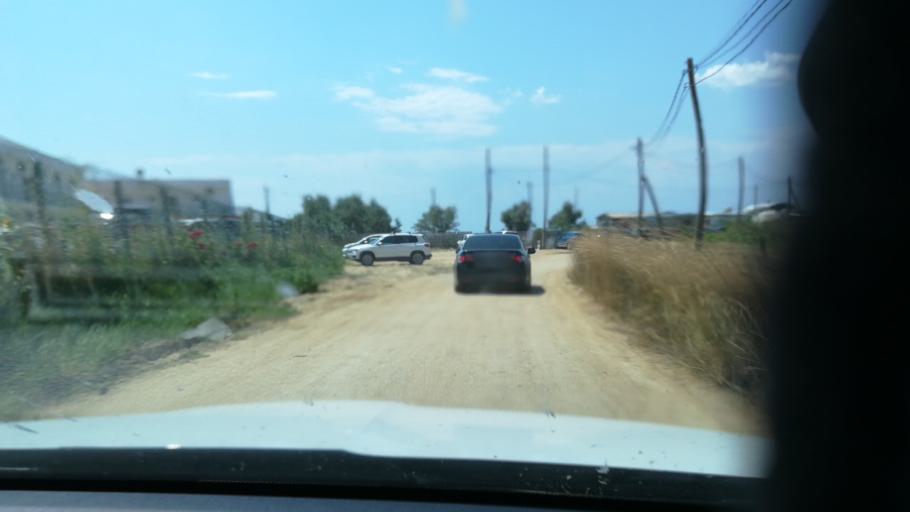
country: RU
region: Krasnodarskiy
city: Vyshestebliyevskaya
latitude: 45.1127
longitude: 36.8732
